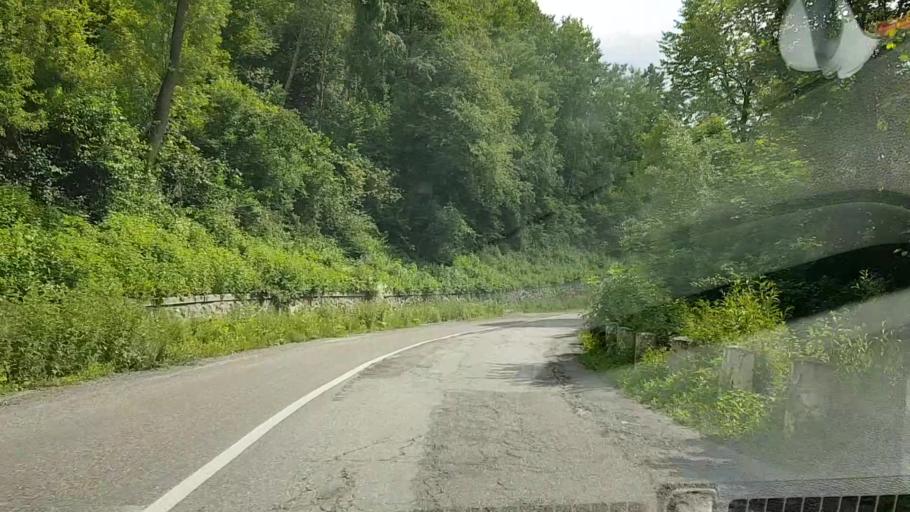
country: RO
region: Neamt
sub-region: Comuna Ceahlau
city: Ceahlau
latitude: 47.0743
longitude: 25.9638
